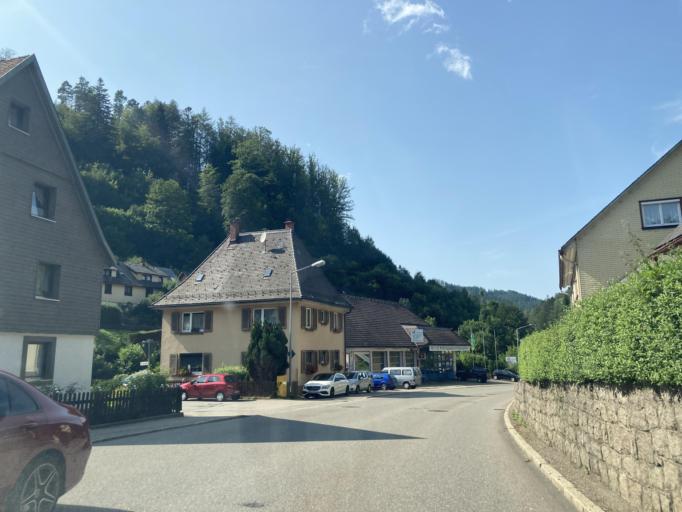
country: DE
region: Baden-Wuerttemberg
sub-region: Freiburg Region
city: Triberg im Schwarzwald
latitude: 48.1345
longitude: 8.2463
